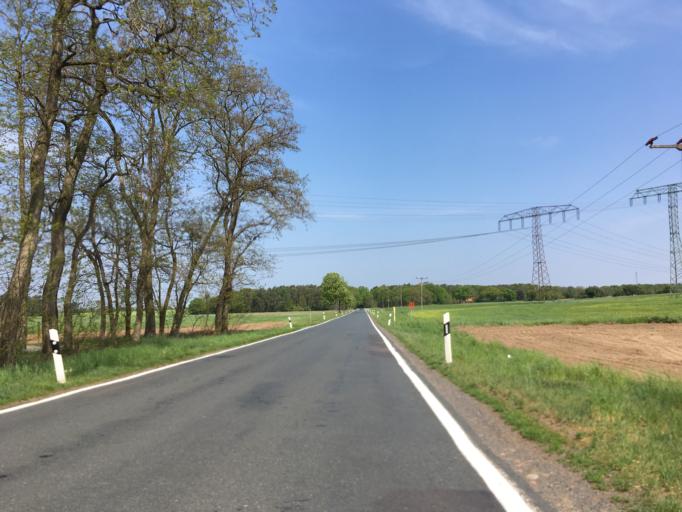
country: DE
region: Brandenburg
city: Melchow
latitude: 52.7183
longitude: 13.7135
